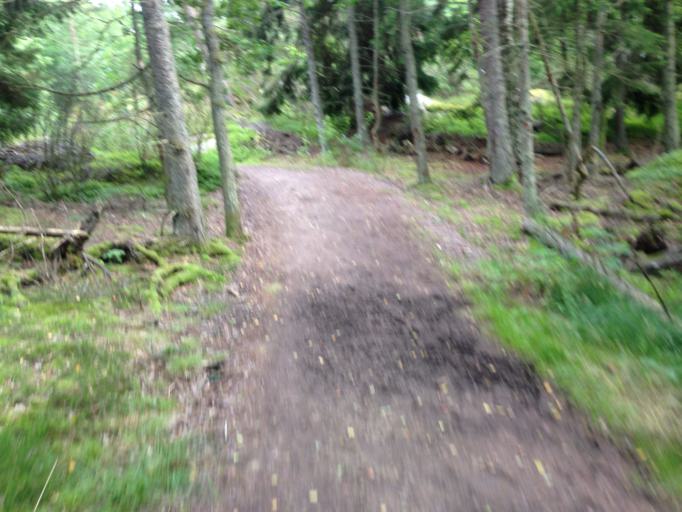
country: SE
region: Vaestra Goetaland
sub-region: Kungalvs Kommun
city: Kungalv
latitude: 57.8151
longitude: 11.8883
